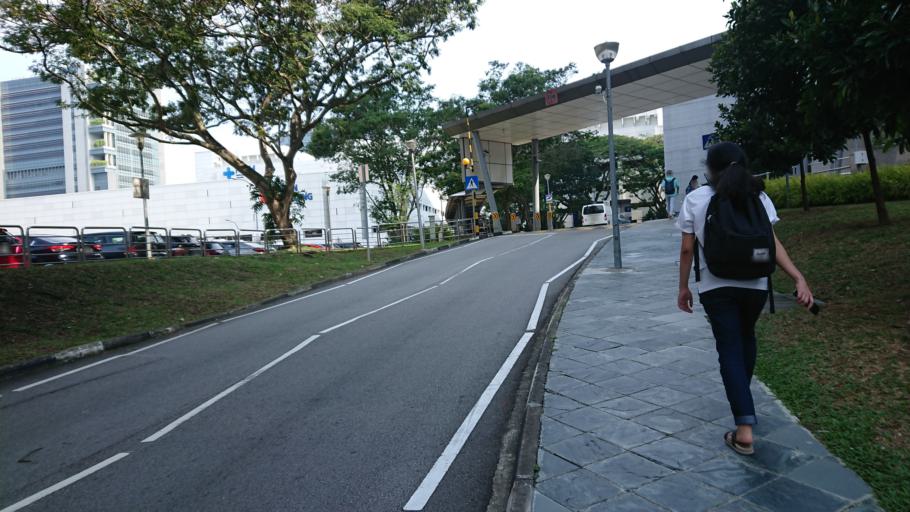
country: SG
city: Singapore
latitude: 1.2959
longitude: 103.7819
